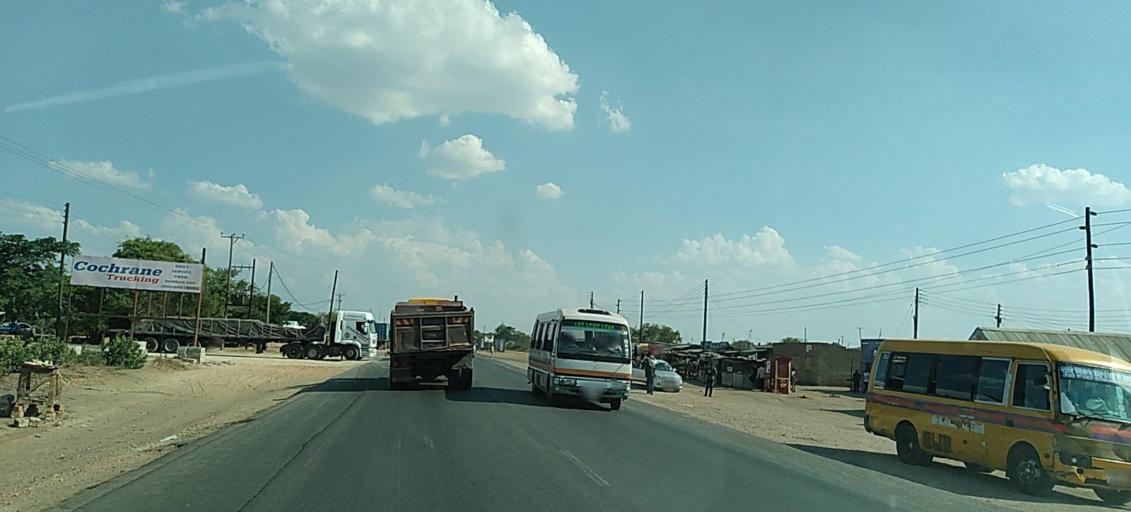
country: ZM
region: Lusaka
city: Lusaka
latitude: -15.2290
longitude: 28.2549
